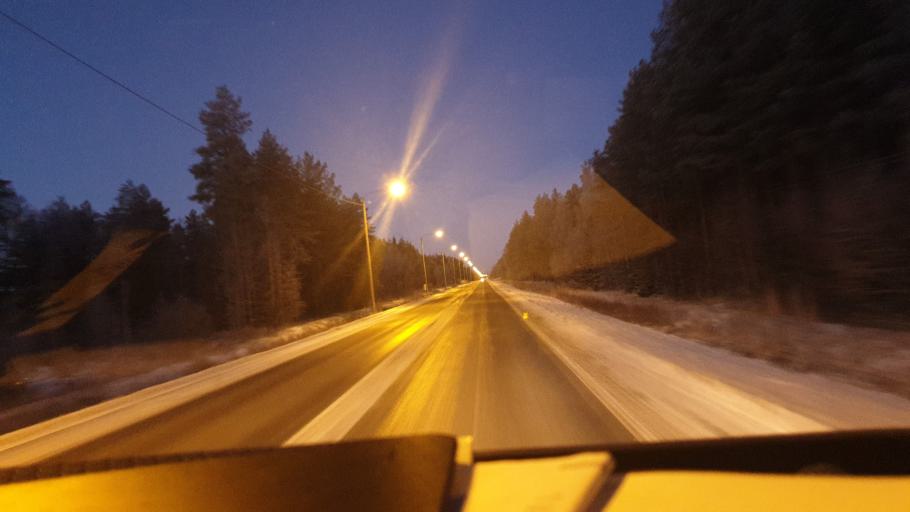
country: FI
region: Northern Ostrobothnia
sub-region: Raahe
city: Raahe
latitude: 64.6911
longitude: 24.6409
